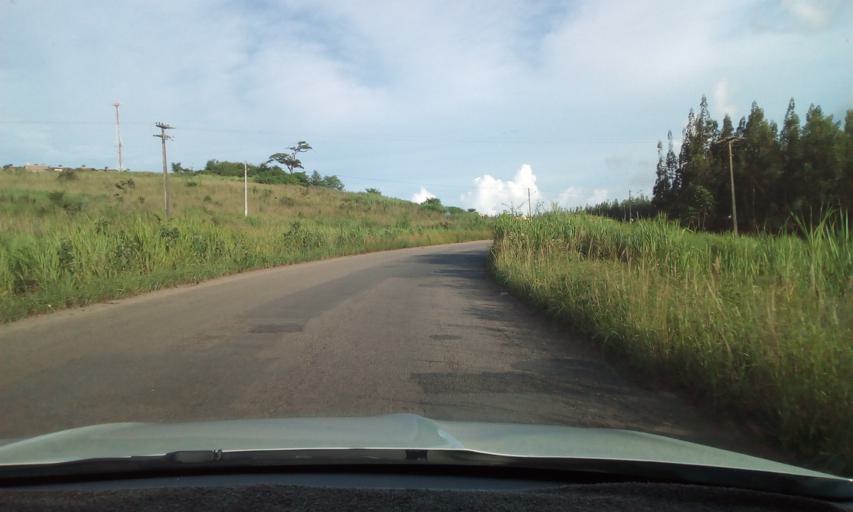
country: BR
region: Pernambuco
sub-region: Gloria Do Goita
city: Gloria do Goita
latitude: -7.9956
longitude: -35.2251
